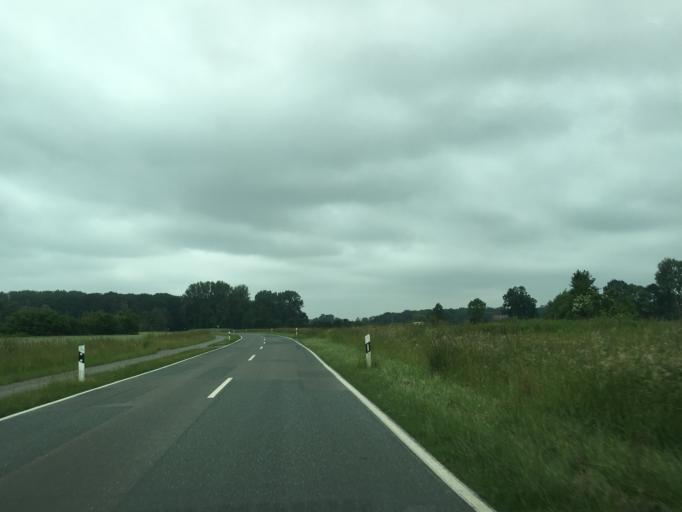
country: DE
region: North Rhine-Westphalia
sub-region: Regierungsbezirk Munster
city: Altenberge
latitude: 52.0063
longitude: 7.4908
